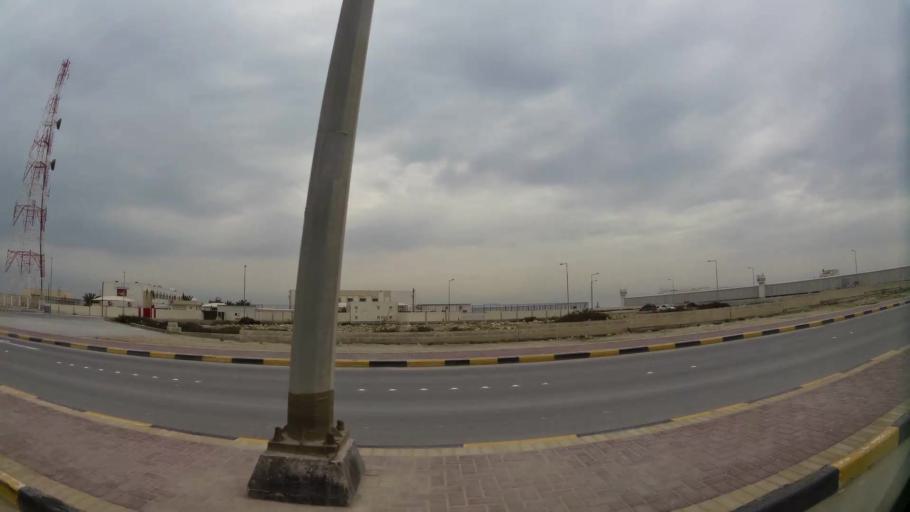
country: BH
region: Central Governorate
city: Dar Kulayb
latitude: 25.9965
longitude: 50.6168
